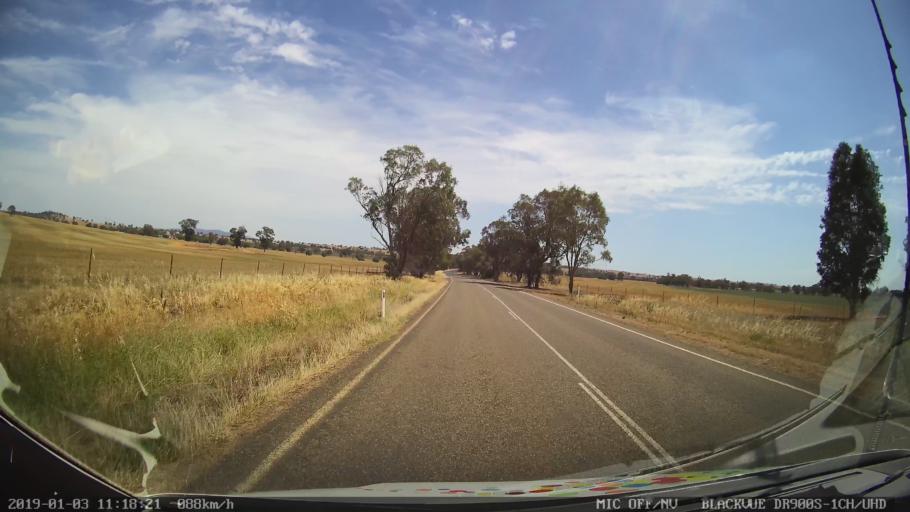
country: AU
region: New South Wales
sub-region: Young
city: Young
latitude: -34.1272
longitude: 148.2630
